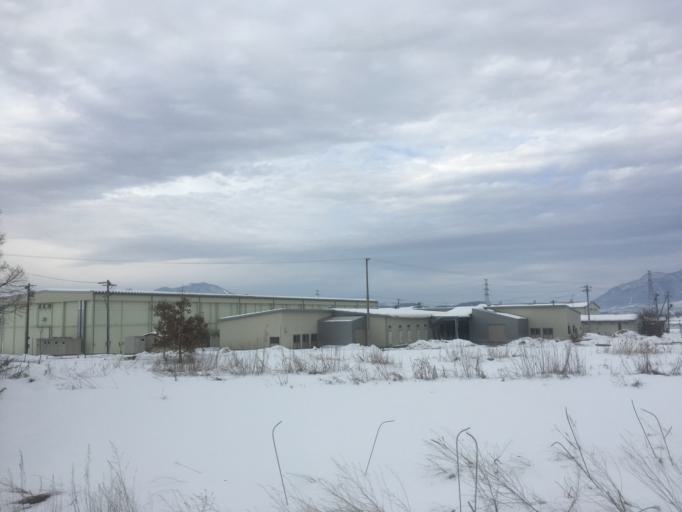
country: JP
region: Nagano
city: Nakano
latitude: 36.7093
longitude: 138.3389
